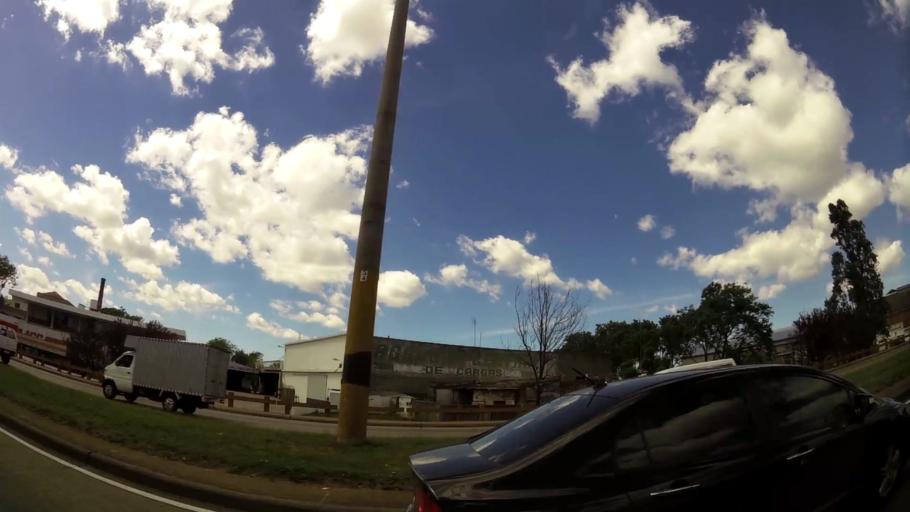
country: UY
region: Montevideo
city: Montevideo
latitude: -34.8734
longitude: -56.2065
